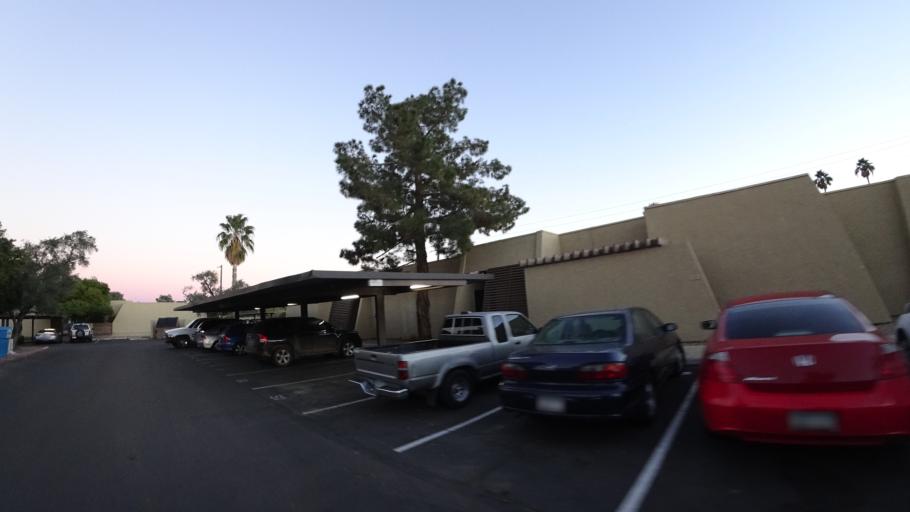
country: US
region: Arizona
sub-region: Maricopa County
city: Tempe Junction
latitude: 33.4138
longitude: -111.9510
